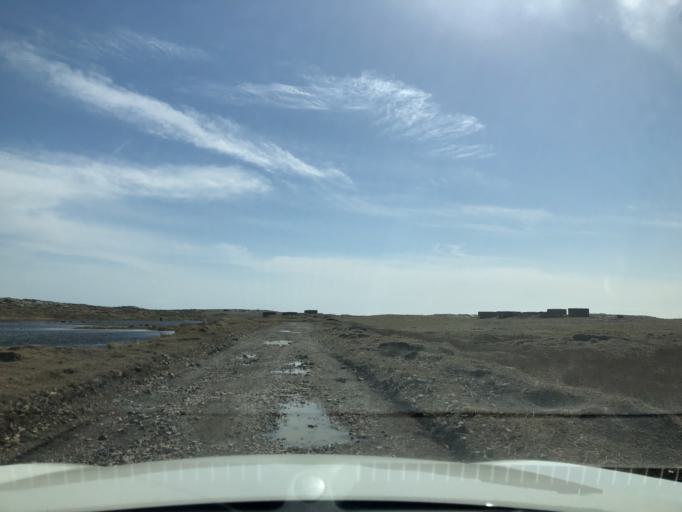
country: IS
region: East
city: Hoefn
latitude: 64.2424
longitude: -14.9717
